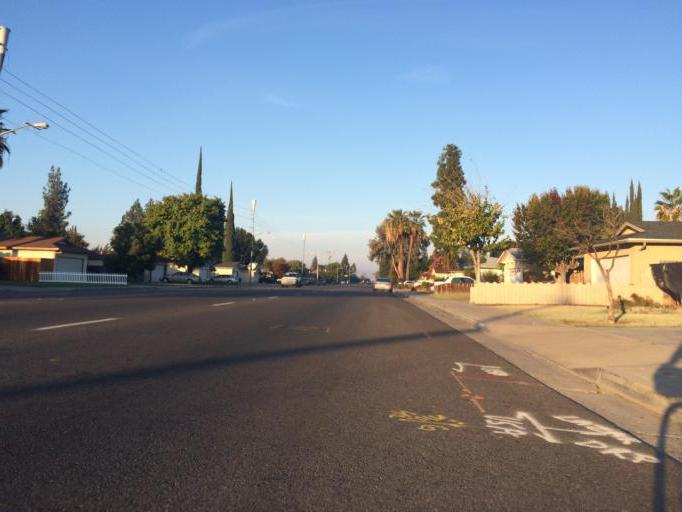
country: US
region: California
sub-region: Fresno County
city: Tarpey Village
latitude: 36.8013
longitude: -119.7230
